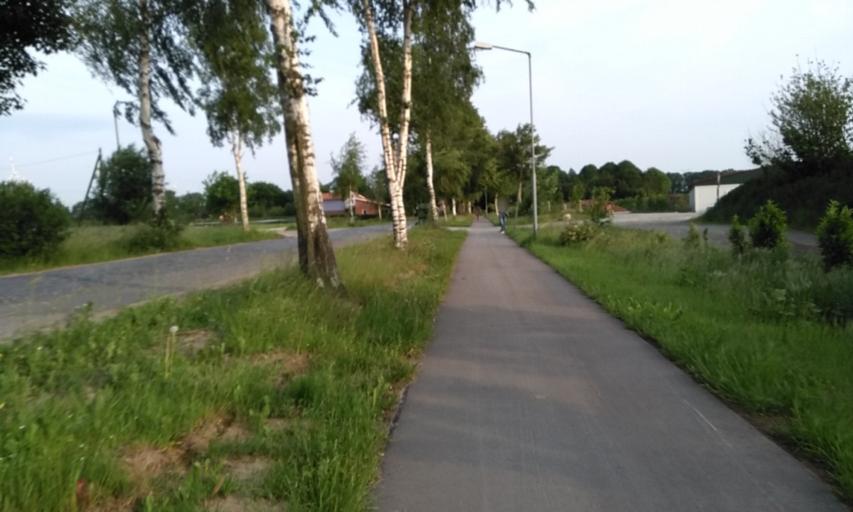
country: DE
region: Lower Saxony
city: Deinste
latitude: 53.5223
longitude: 9.4435
